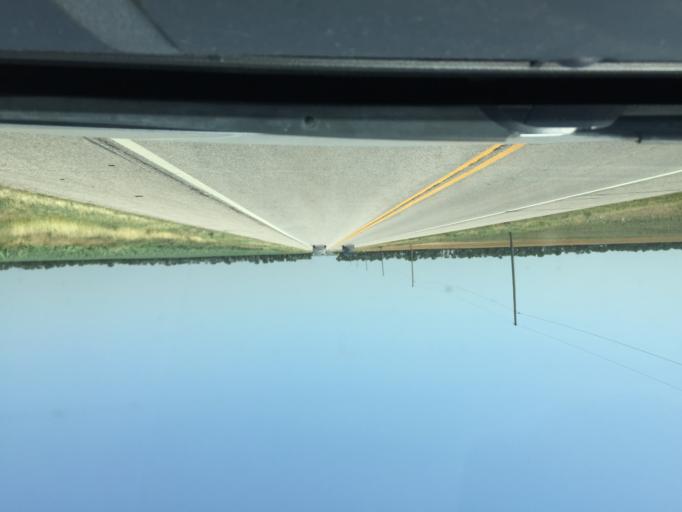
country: US
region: Kansas
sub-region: Reno County
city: South Hutchinson
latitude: 38.0138
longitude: -97.8669
